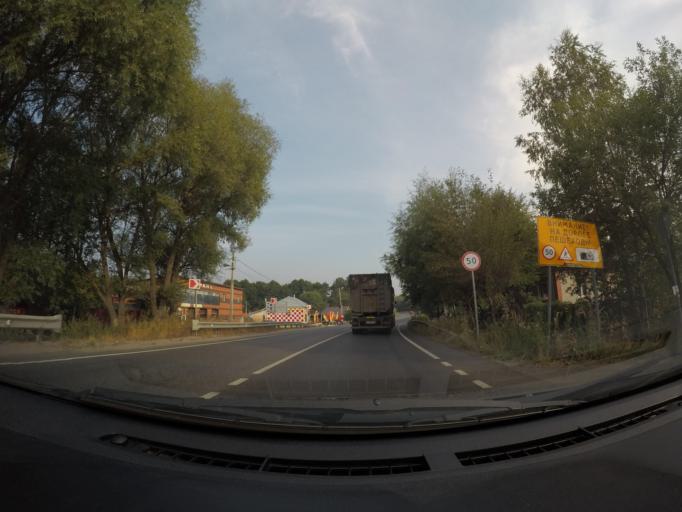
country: RU
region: Moskovskaya
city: Rechitsy
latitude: 55.5795
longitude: 38.5697
